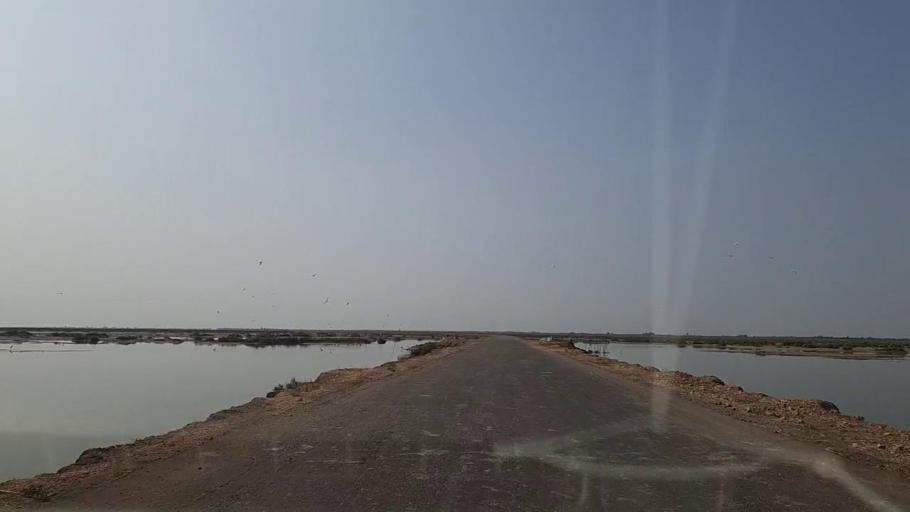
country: PK
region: Sindh
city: Chuhar Jamali
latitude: 24.2239
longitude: 67.8830
